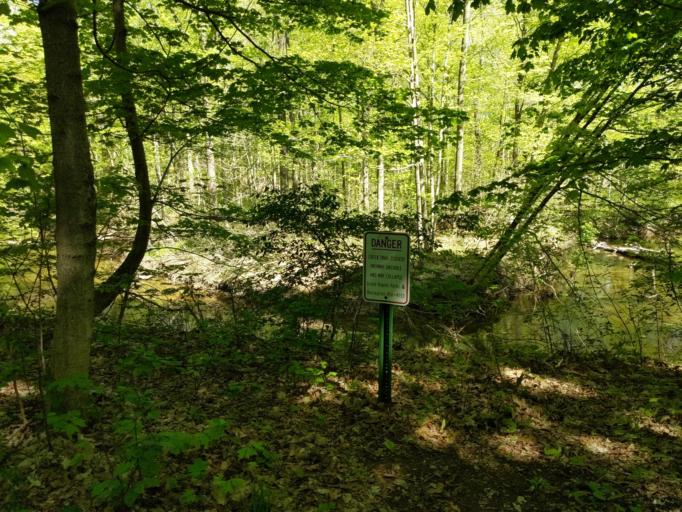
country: US
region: Michigan
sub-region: Kent County
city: Kentwood
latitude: 42.9058
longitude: -85.6332
